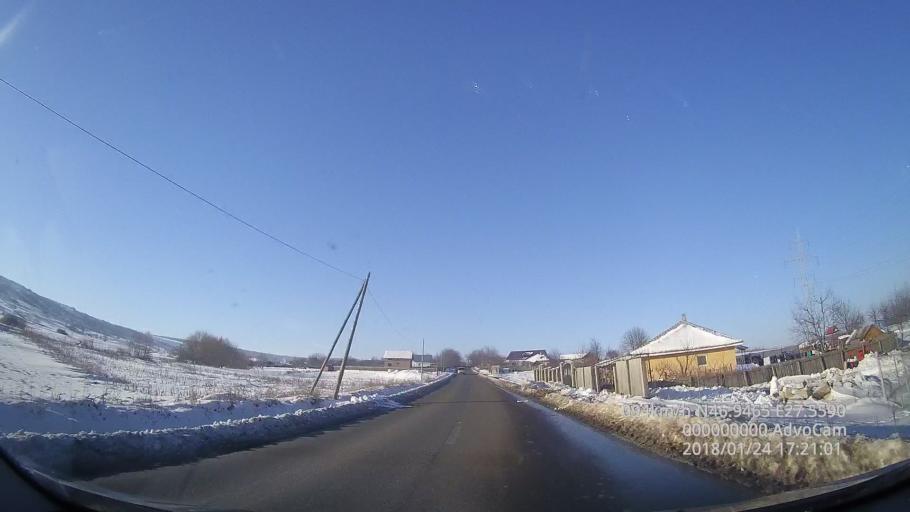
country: RO
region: Iasi
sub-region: Comuna Scanteia
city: Scanteia
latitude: 46.9472
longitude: 27.5584
